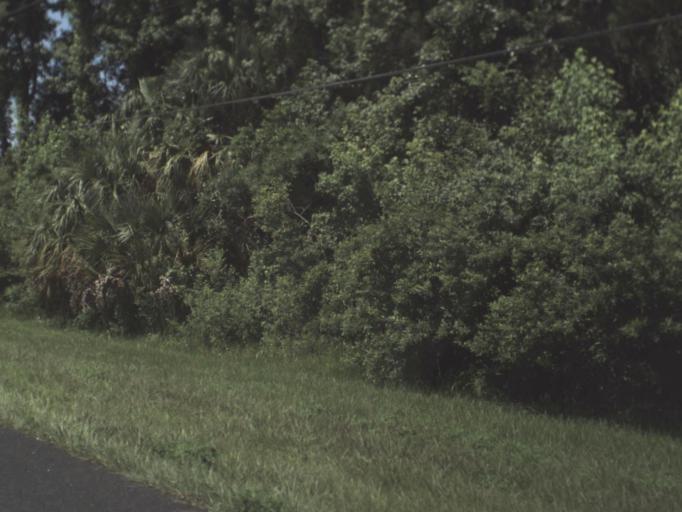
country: US
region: Florida
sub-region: Citrus County
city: Homosassa Springs
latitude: 28.8193
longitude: -82.5778
